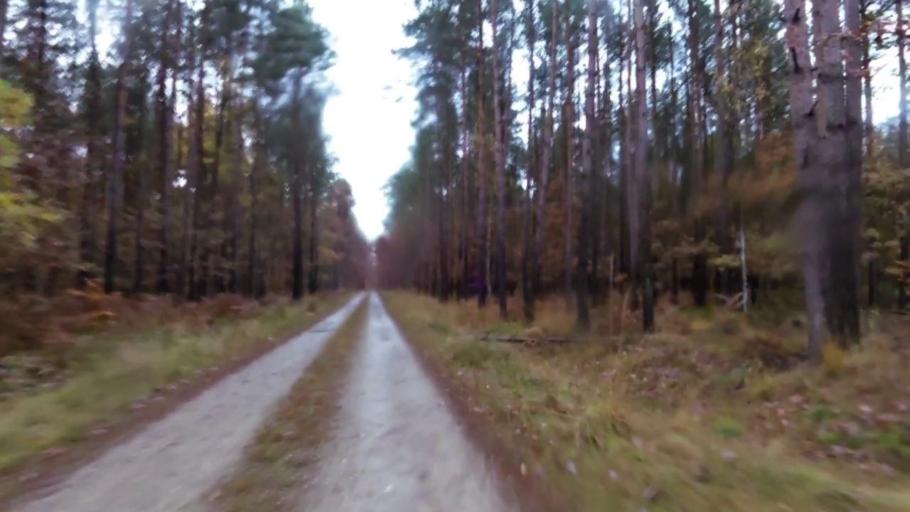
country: PL
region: West Pomeranian Voivodeship
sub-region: Powiat goleniowski
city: Stepnica
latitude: 53.6490
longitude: 14.6975
